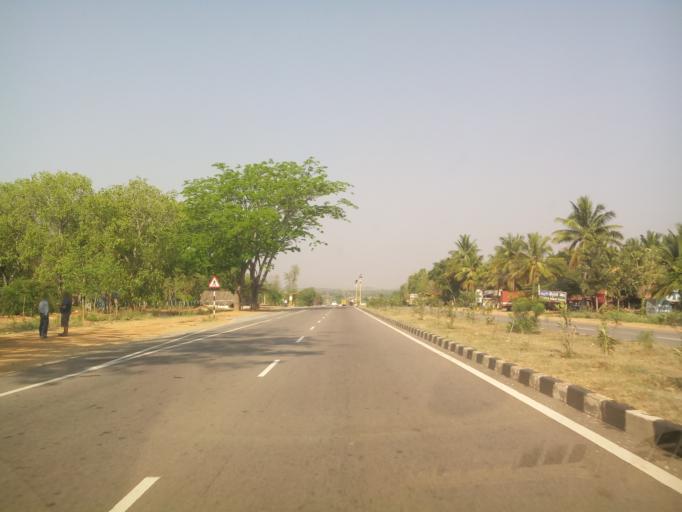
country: IN
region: Karnataka
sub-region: Tumkur
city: Kunigal
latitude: 12.9969
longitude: 76.9194
